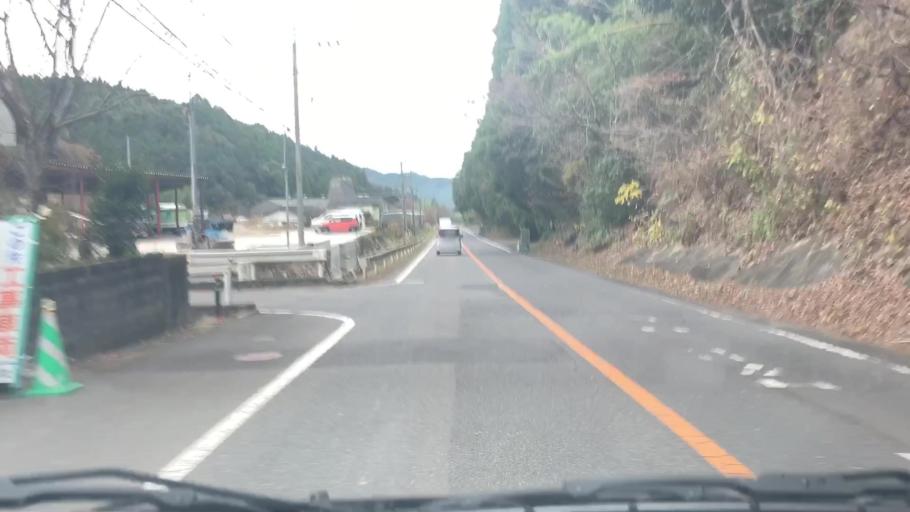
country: JP
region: Saga Prefecture
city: Takeocho-takeo
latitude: 33.1839
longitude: 129.9695
